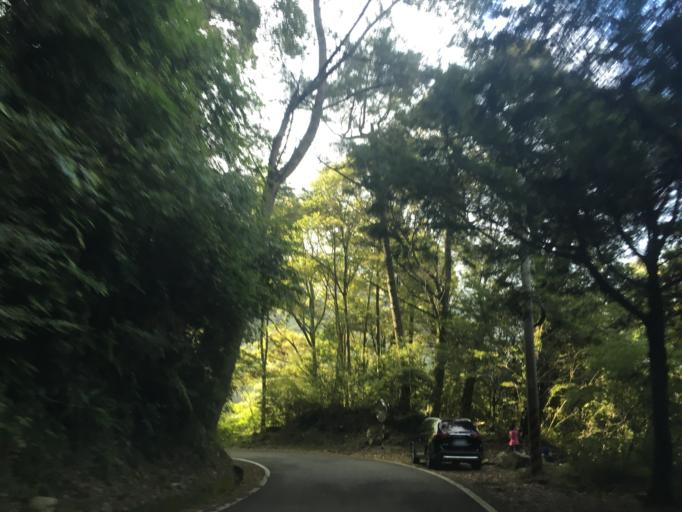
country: TW
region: Taiwan
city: Fengyuan
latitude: 24.2357
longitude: 120.9782
